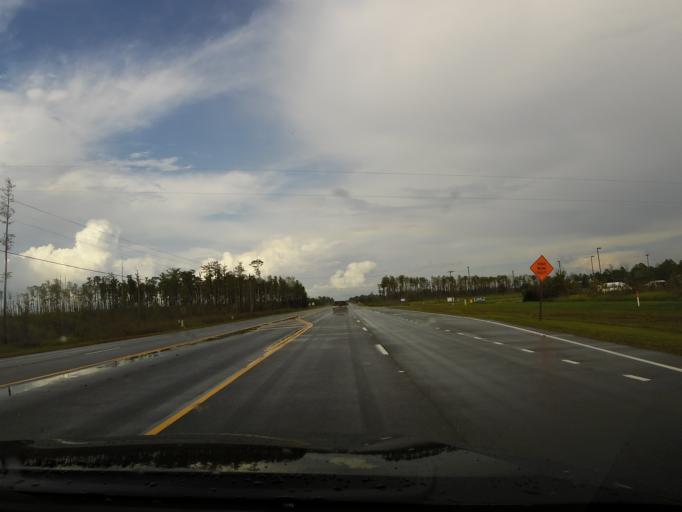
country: US
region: Georgia
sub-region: Long County
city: Ludowici
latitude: 31.7234
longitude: -81.7268
